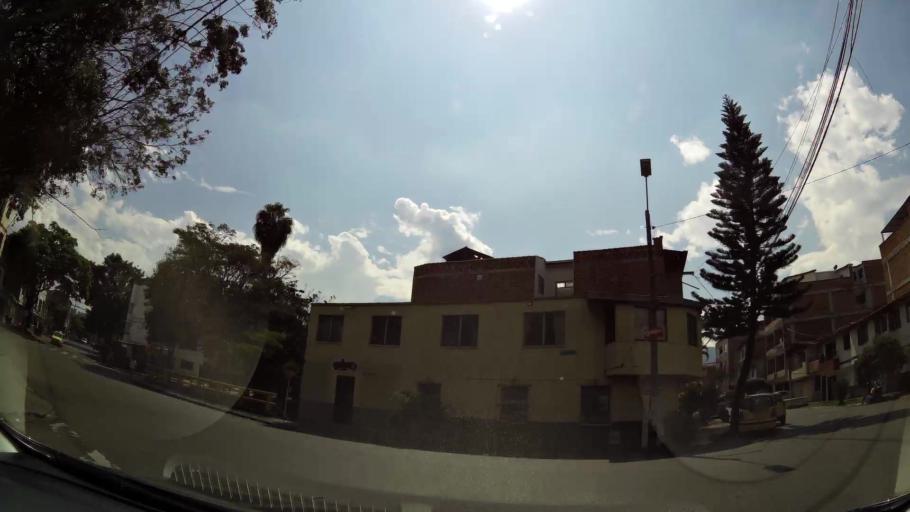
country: CO
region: Antioquia
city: Medellin
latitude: 6.2288
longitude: -75.5927
